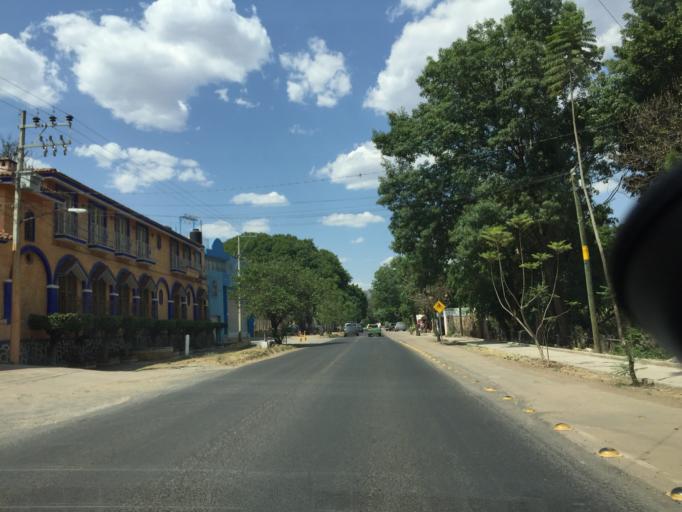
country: MX
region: Jalisco
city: Atotonilco el Alto
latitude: 20.5550
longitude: -102.4951
